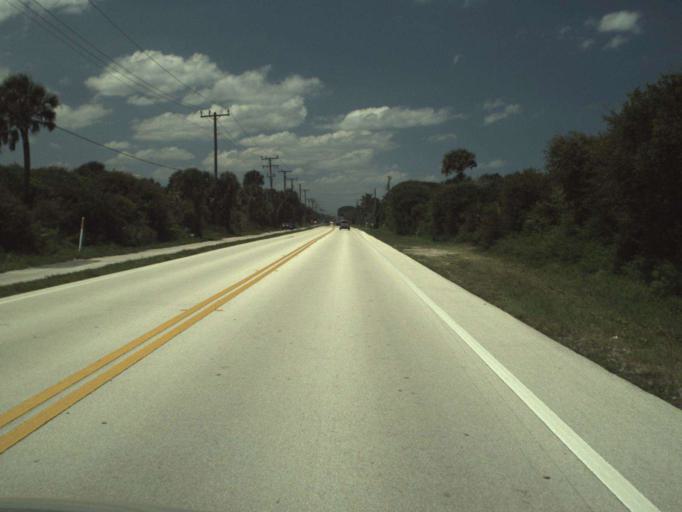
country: US
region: Florida
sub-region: Brevard County
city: Grant-Valkaria
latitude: 27.9573
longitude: -80.5031
